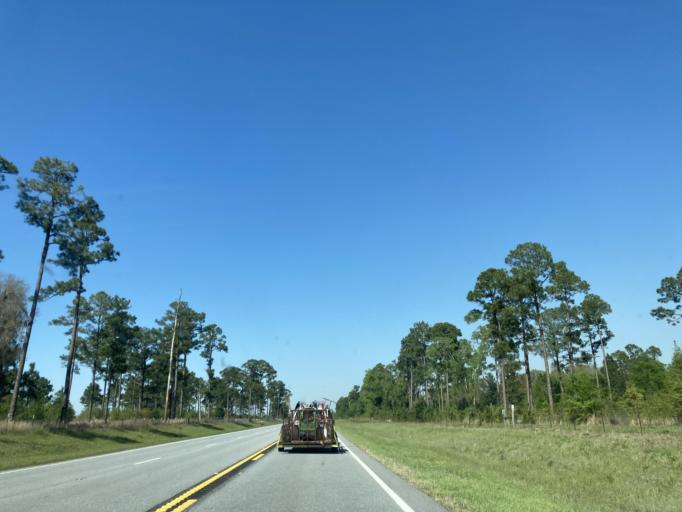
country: US
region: Georgia
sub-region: Dougherty County
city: Putney
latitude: 31.4502
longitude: -84.2614
